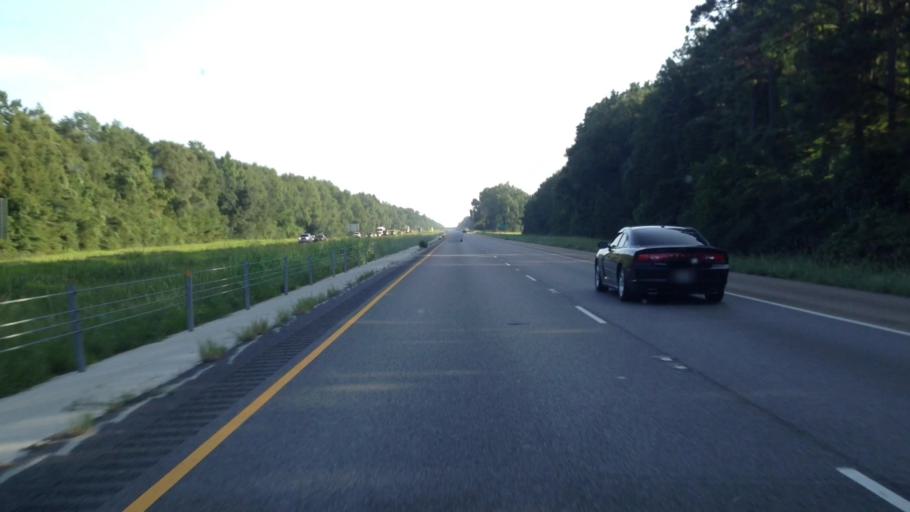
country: US
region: Louisiana
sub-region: Tangipahoa Parish
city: Natalbany
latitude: 30.5296
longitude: -90.5038
